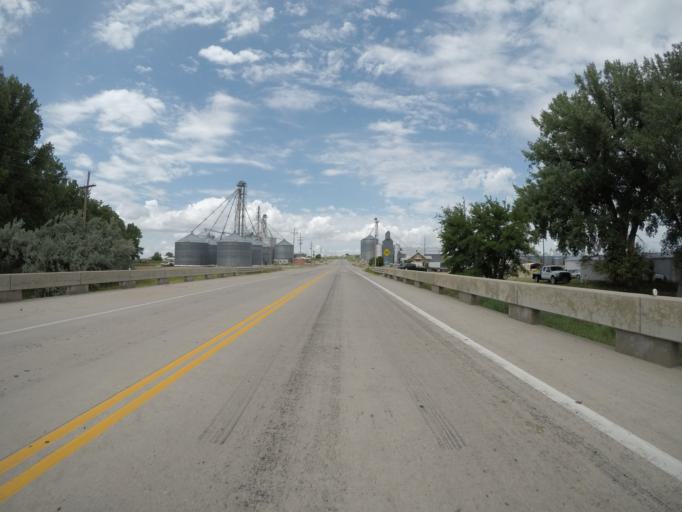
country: US
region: Kansas
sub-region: Rawlins County
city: Atwood
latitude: 39.8213
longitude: -101.0468
